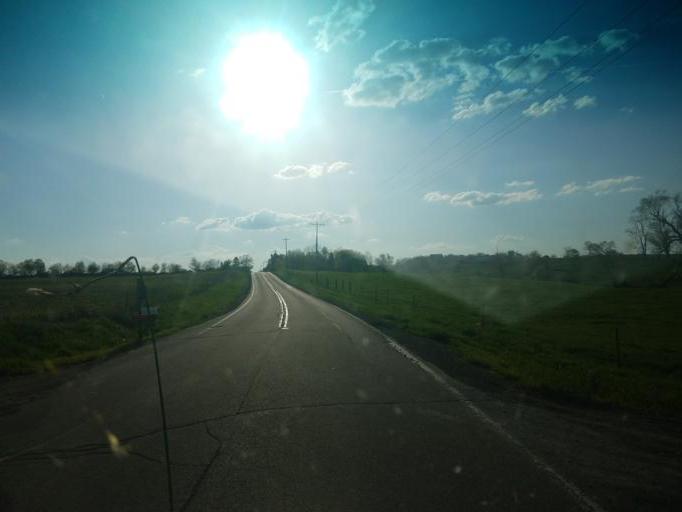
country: US
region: Ohio
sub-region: Wayne County
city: Shreve
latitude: 40.6242
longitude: -82.0386
